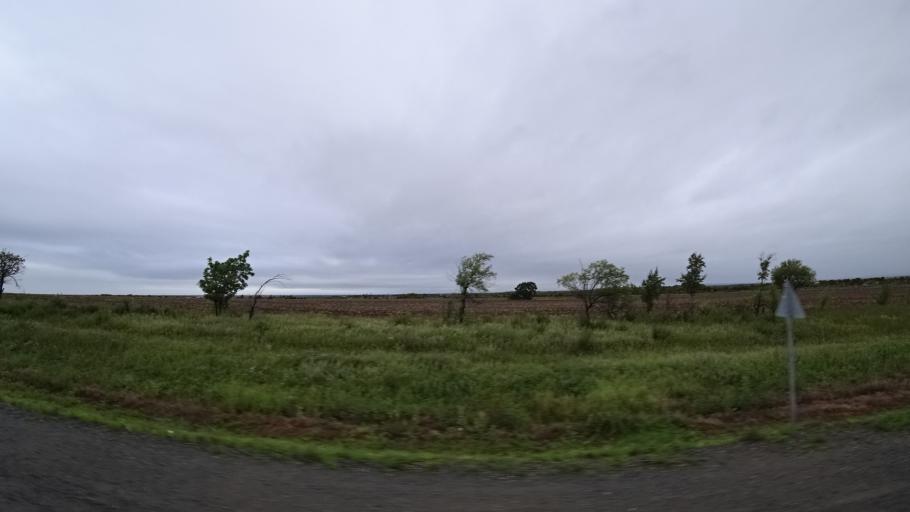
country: RU
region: Primorskiy
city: Chernigovka
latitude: 44.3186
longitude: 132.5652
